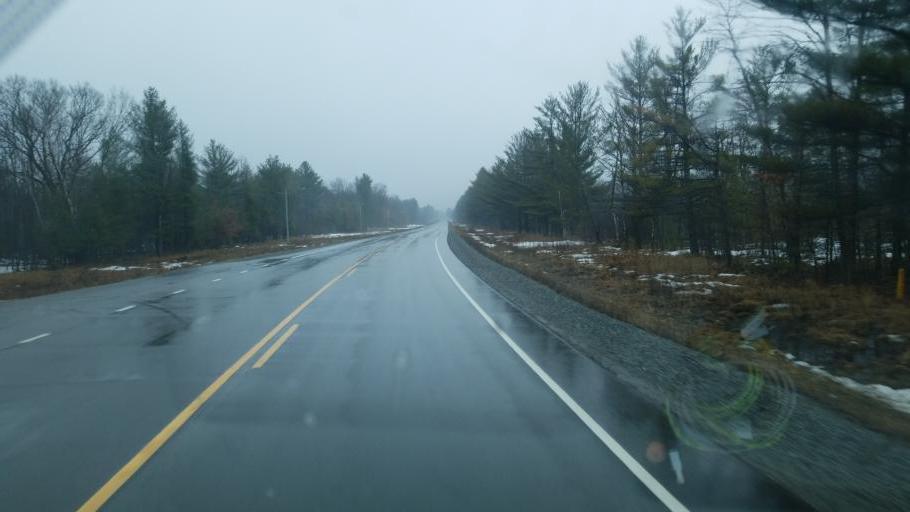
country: US
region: Wisconsin
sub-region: Clark County
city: Neillsville
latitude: 44.4890
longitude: -90.3559
